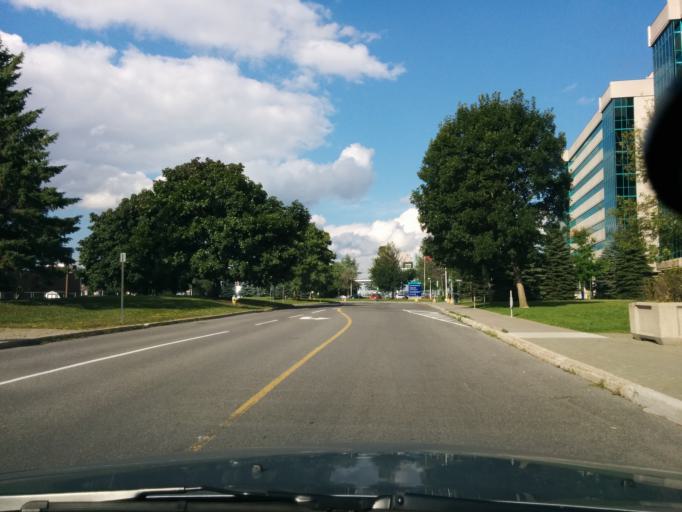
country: CA
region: Ontario
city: Bells Corners
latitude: 45.3457
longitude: -75.7651
